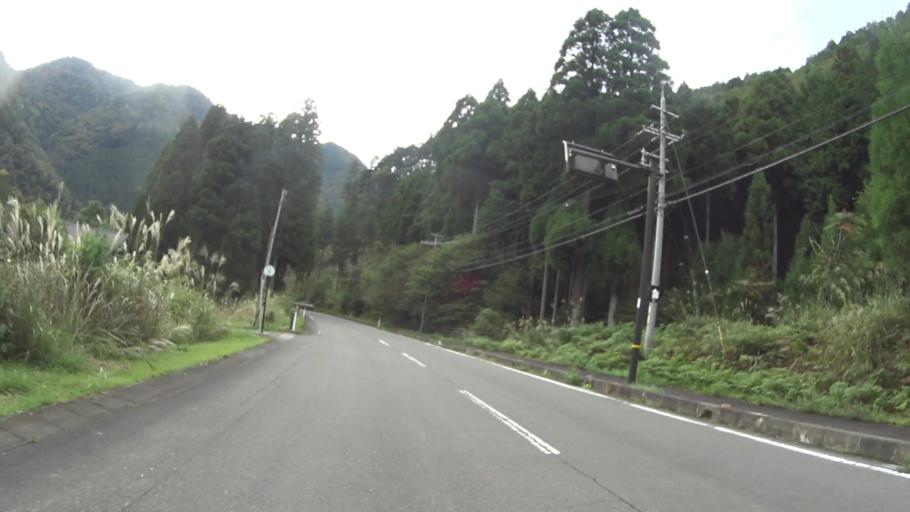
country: JP
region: Fukui
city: Obama
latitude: 35.3238
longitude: 135.6687
